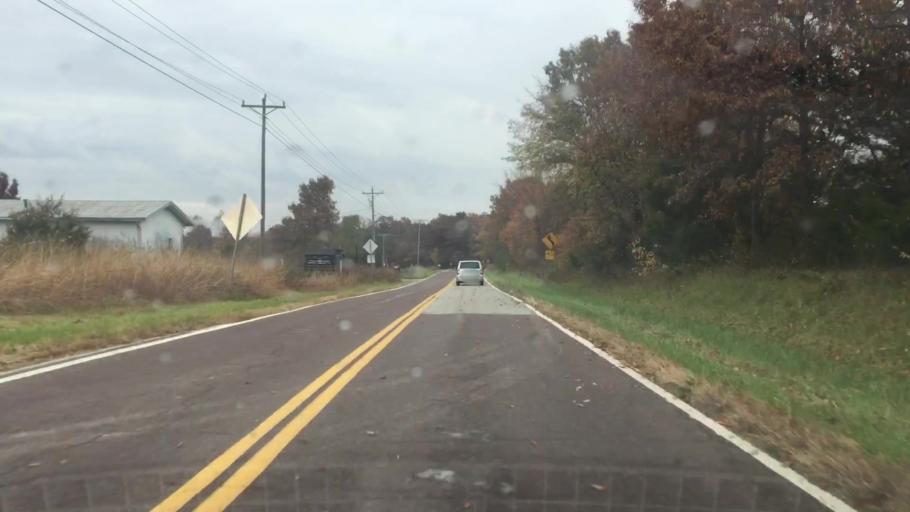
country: US
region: Missouri
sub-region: Callaway County
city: Fulton
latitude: 38.7867
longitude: -91.7943
